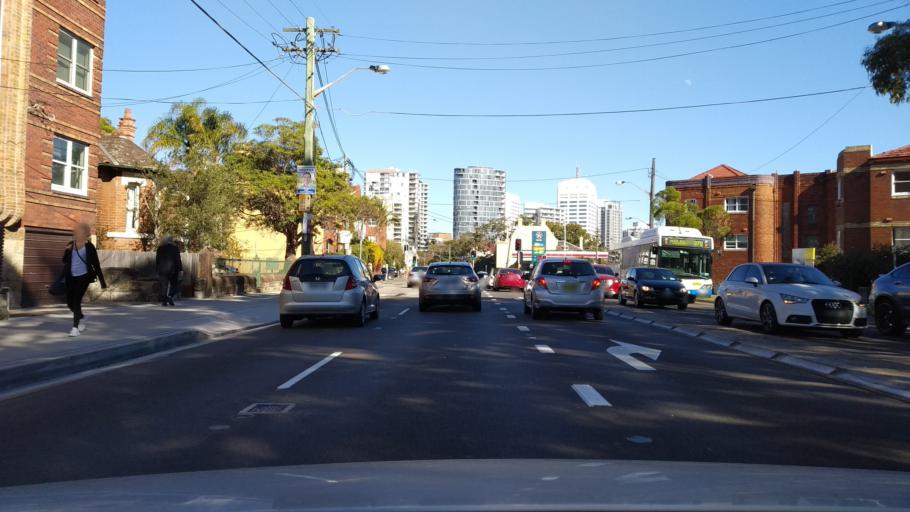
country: AU
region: New South Wales
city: Edgecliff
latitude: -33.8892
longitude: 151.2567
